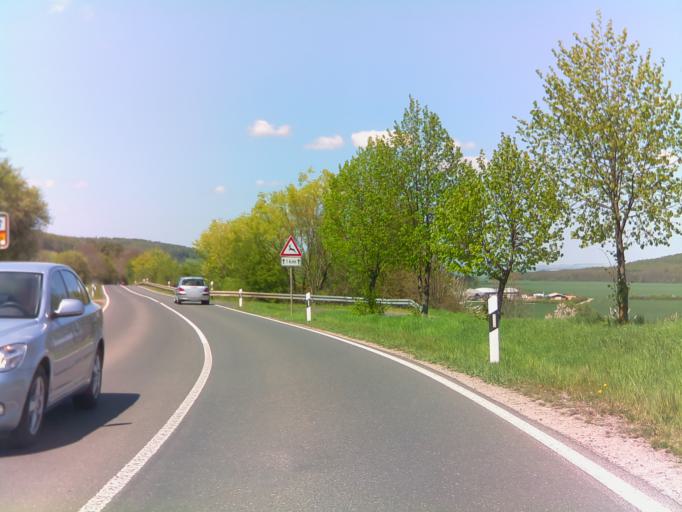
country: DE
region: Thuringia
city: Behringen
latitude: 50.7874
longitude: 10.9920
